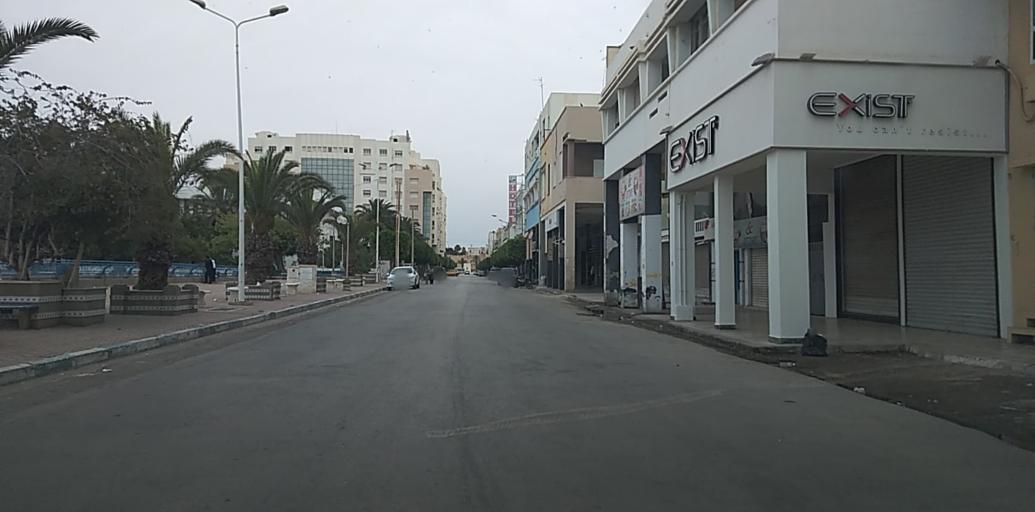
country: TN
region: Safaqis
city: Sfax
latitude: 34.7301
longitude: 10.7636
